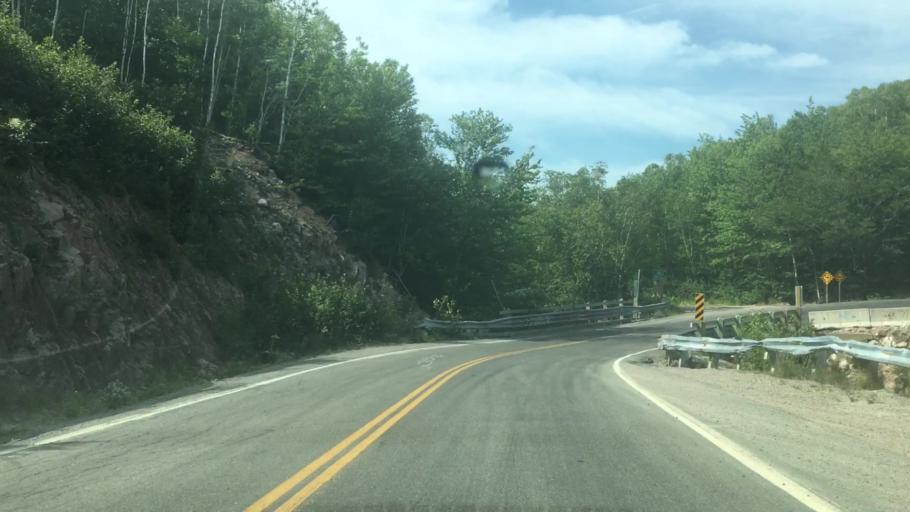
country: CA
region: Nova Scotia
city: Sydney Mines
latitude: 46.5832
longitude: -60.3960
